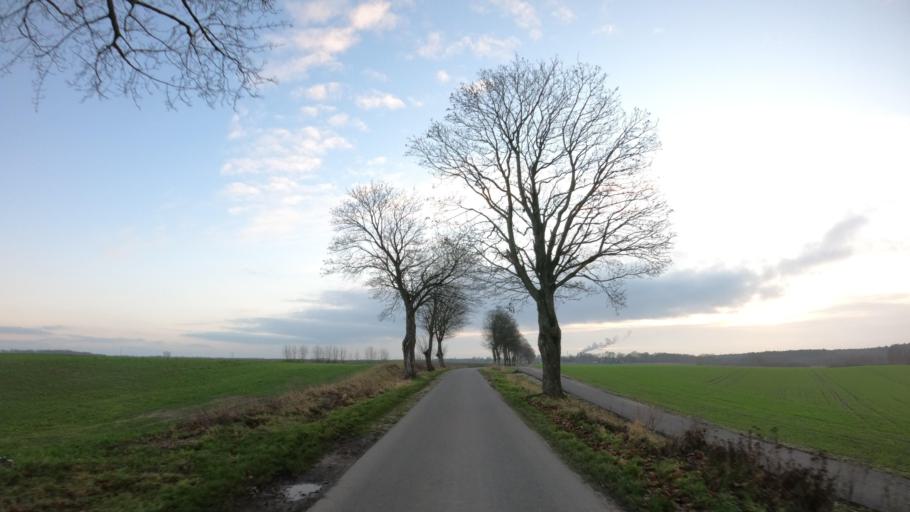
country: PL
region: West Pomeranian Voivodeship
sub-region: Powiat bialogardzki
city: Karlino
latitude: 54.0904
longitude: 15.8858
